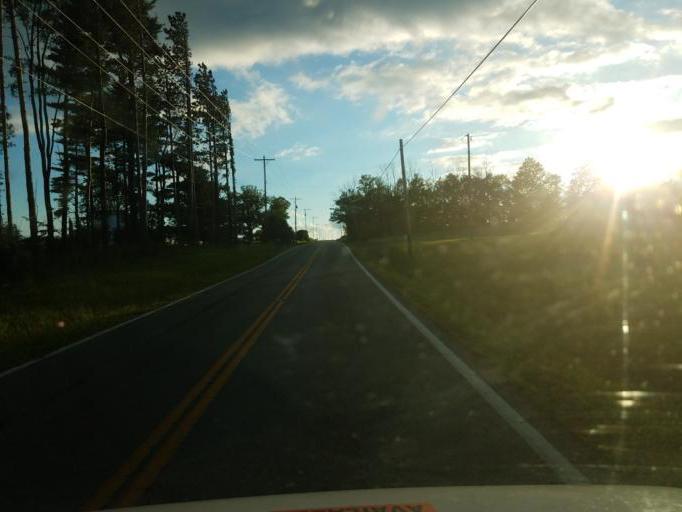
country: US
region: Ohio
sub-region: Knox County
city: Fredericktown
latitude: 40.4032
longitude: -82.5790
